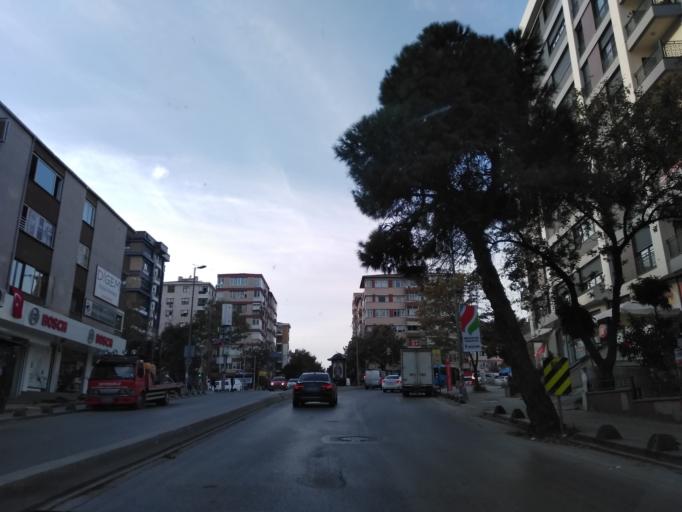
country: TR
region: Istanbul
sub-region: Atasehir
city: Atasehir
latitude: 40.9581
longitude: 29.0960
